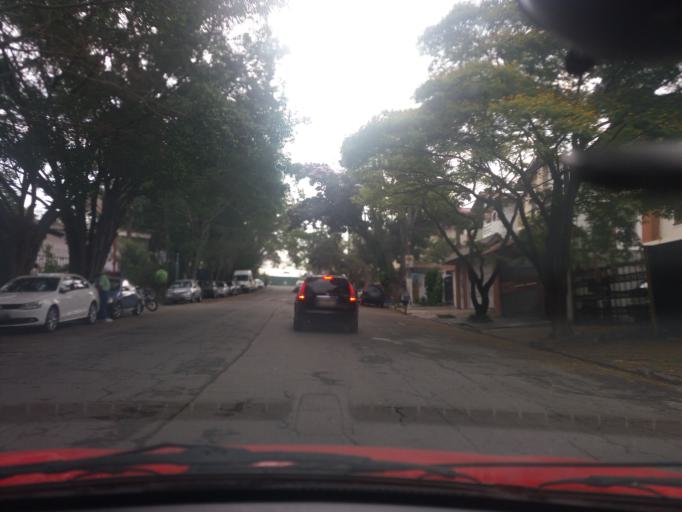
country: BR
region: Sao Paulo
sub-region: Taboao Da Serra
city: Taboao da Serra
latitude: -23.6026
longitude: -46.7290
